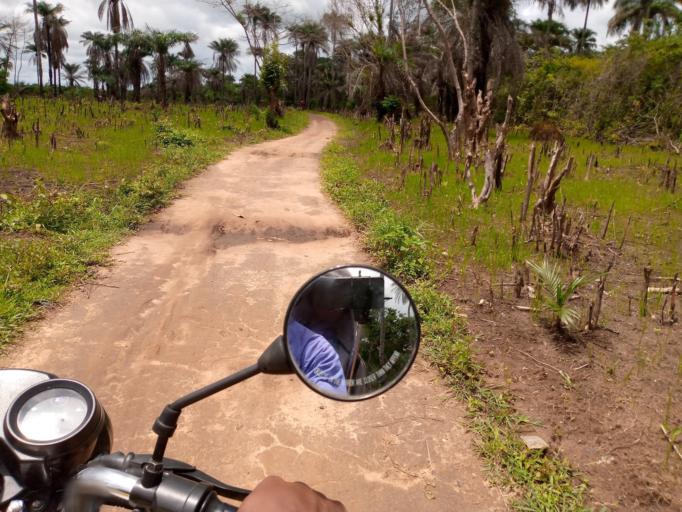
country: SL
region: Northern Province
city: Mange
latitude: 8.9919
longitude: -12.7779
